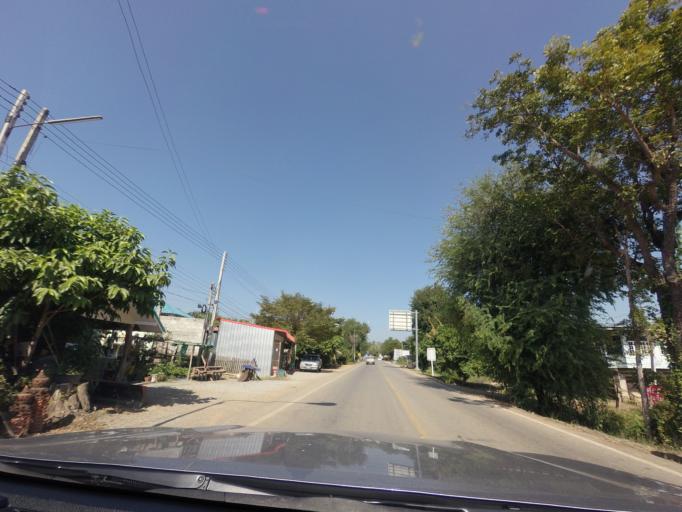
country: TH
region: Sukhothai
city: Sawankhalok
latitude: 17.4000
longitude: 99.7974
